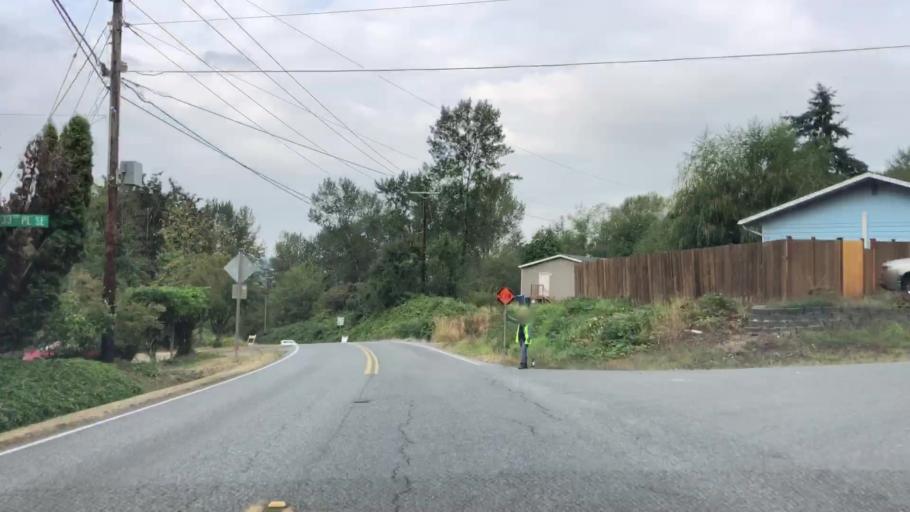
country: US
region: Washington
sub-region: Snohomish County
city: Monroe
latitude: 47.8757
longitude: -121.9889
